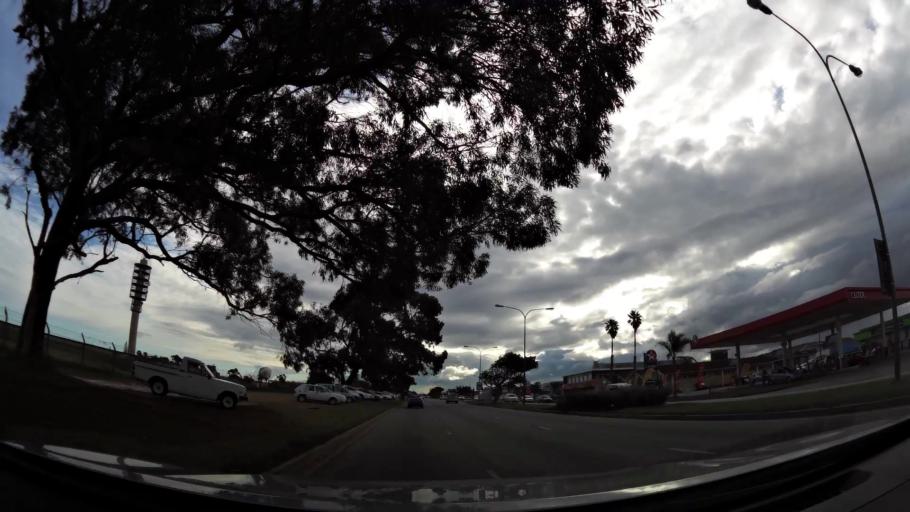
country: ZA
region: Eastern Cape
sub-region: Nelson Mandela Bay Metropolitan Municipality
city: Port Elizabeth
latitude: -33.9447
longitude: 25.5161
